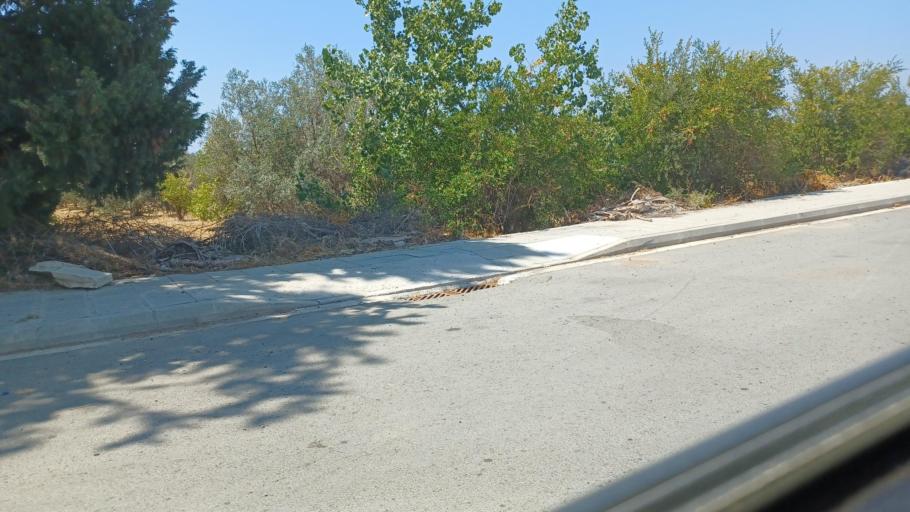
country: CY
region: Pafos
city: Paphos
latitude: 34.7372
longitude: 32.4853
